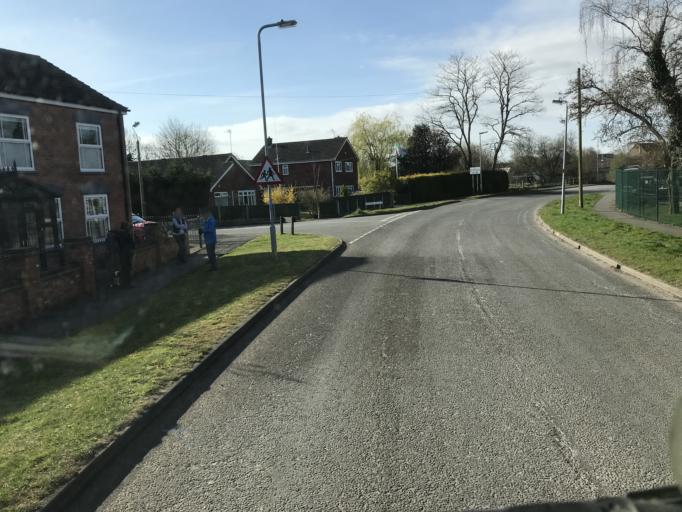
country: GB
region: England
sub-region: Lincolnshire
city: Market Rasen
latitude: 53.3894
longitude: -0.3312
